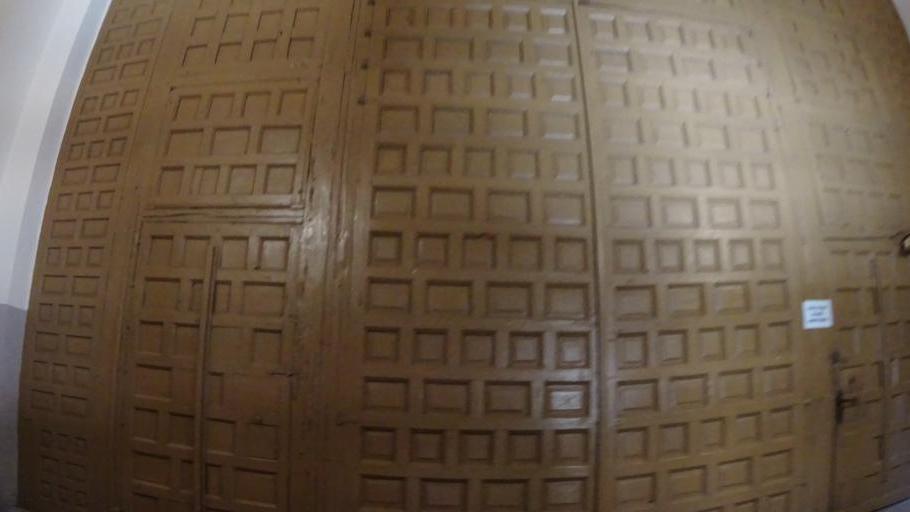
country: ES
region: Castille and Leon
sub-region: Provincia de Segovia
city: Pradena
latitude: 41.1401
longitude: -3.6889
